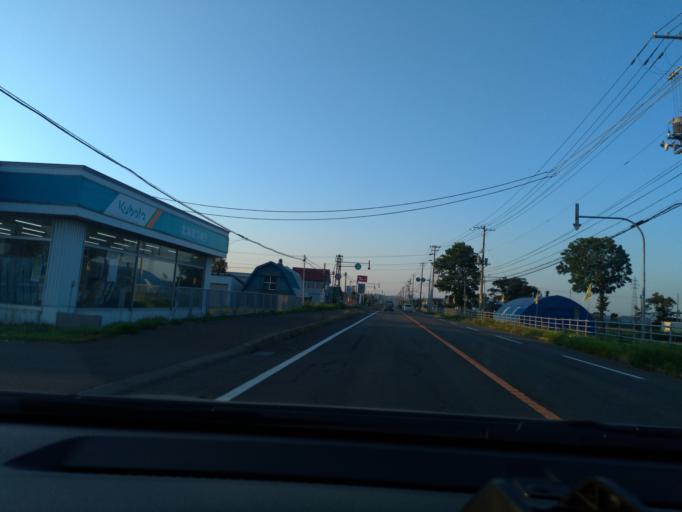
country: JP
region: Hokkaido
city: Tobetsu
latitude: 43.1990
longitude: 141.5223
